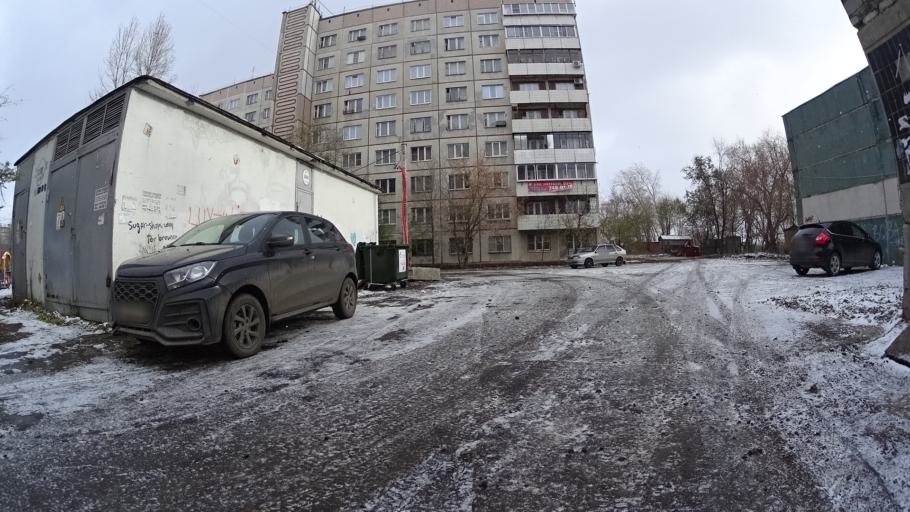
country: RU
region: Chelyabinsk
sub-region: Gorod Chelyabinsk
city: Chelyabinsk
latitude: 55.1880
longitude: 61.3150
